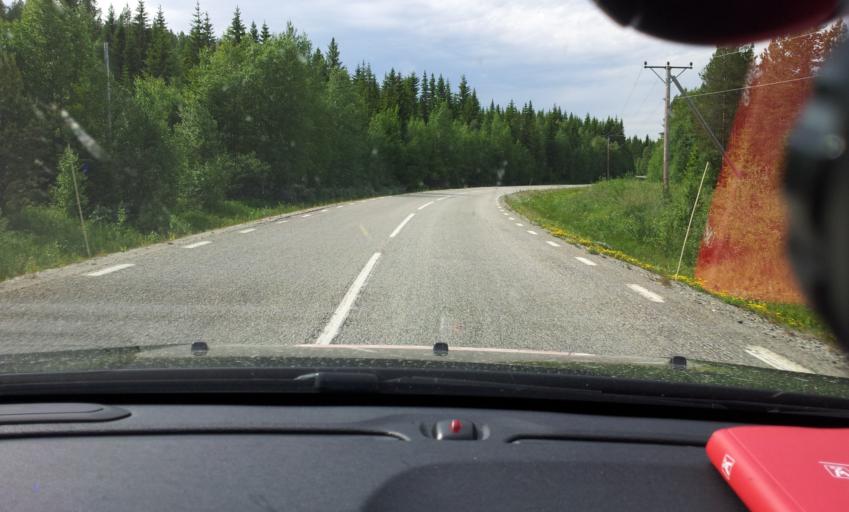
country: SE
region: Jaemtland
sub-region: OEstersunds Kommun
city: Brunflo
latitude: 62.6573
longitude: 14.8775
